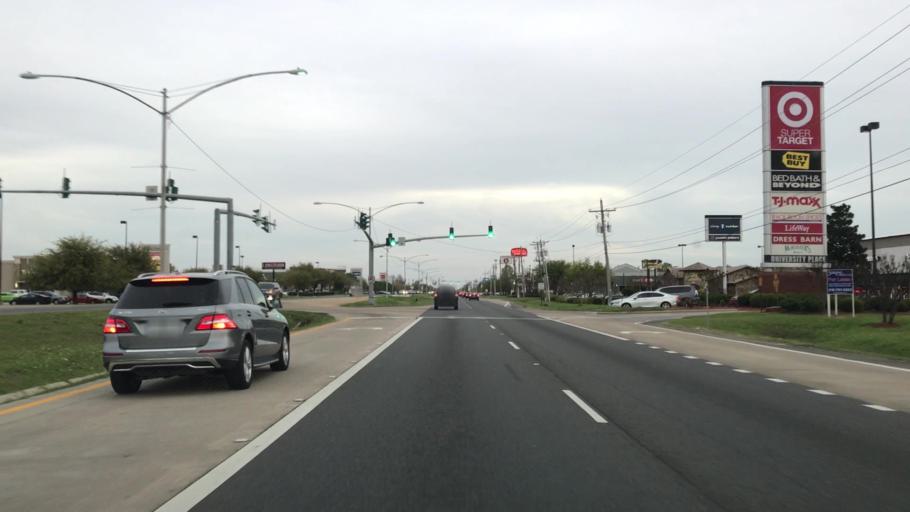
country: US
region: Louisiana
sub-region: Bossier Parish
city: Bossier City
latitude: 32.4418
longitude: -93.7178
